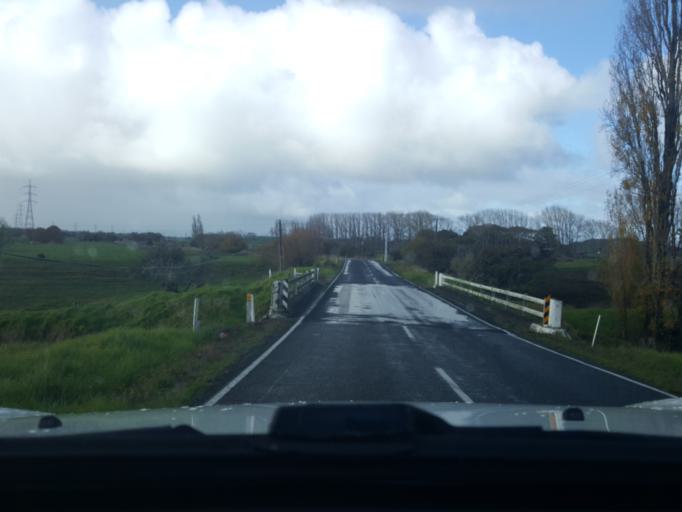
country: NZ
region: Waikato
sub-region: Waikato District
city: Te Kauwhata
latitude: -37.4448
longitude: 175.0876
